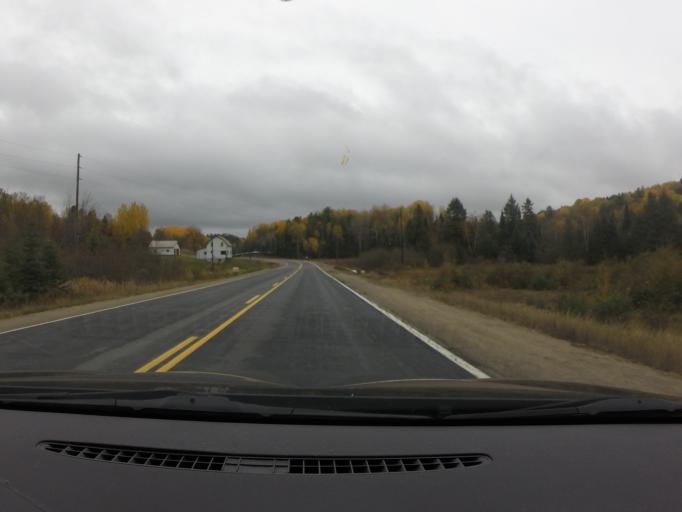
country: CA
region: Ontario
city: Bancroft
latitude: 45.1045
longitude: -77.6394
